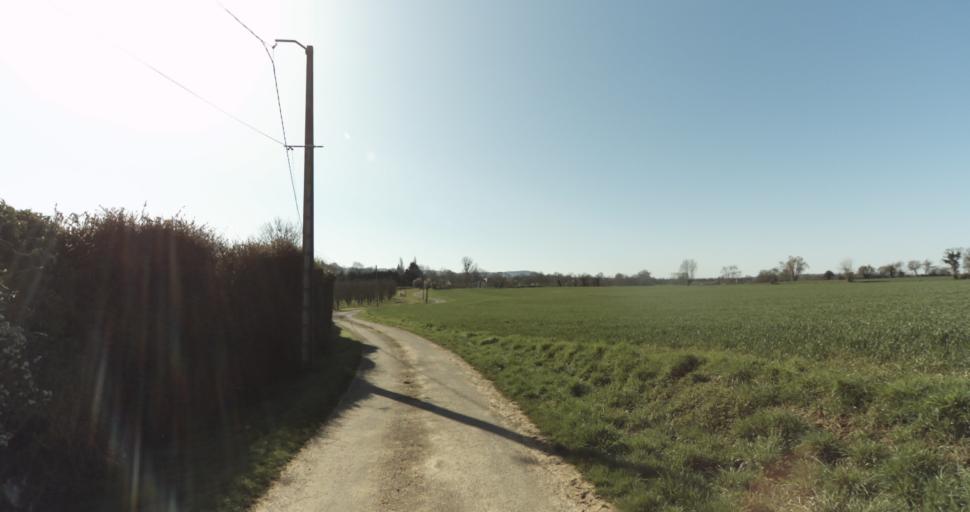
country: FR
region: Lower Normandy
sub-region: Departement du Calvados
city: Saint-Pierre-sur-Dives
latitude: 48.9474
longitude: 0.0272
